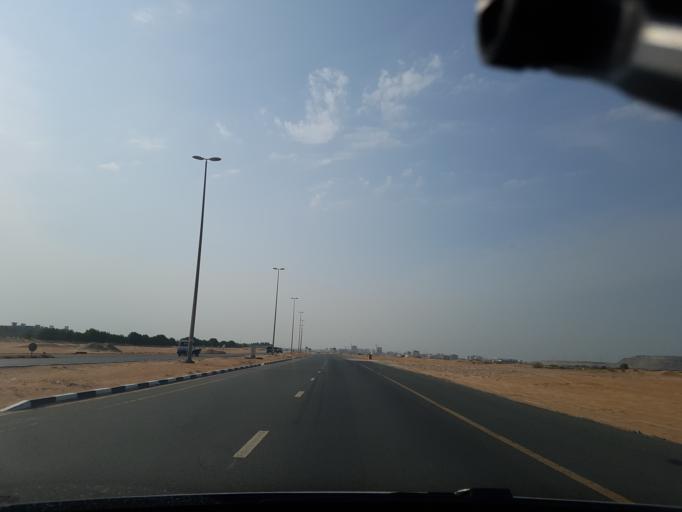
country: AE
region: Ajman
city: Ajman
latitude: 25.4104
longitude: 55.5679
